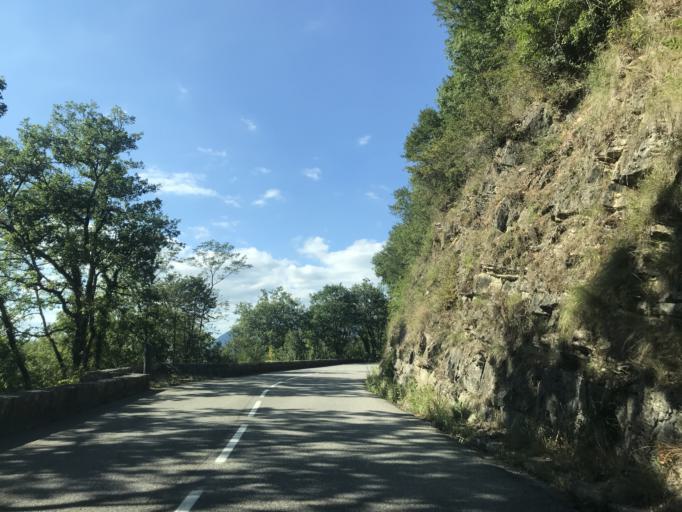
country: FR
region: Rhone-Alpes
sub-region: Departement de l'Ain
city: Culoz
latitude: 45.7941
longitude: 5.7855
